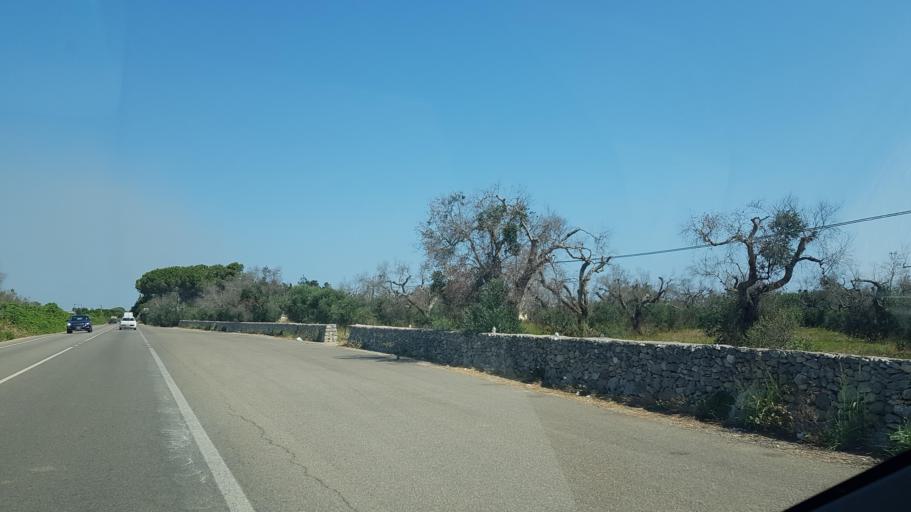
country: IT
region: Apulia
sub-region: Provincia di Lecce
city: Otranto
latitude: 40.1600
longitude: 18.4730
